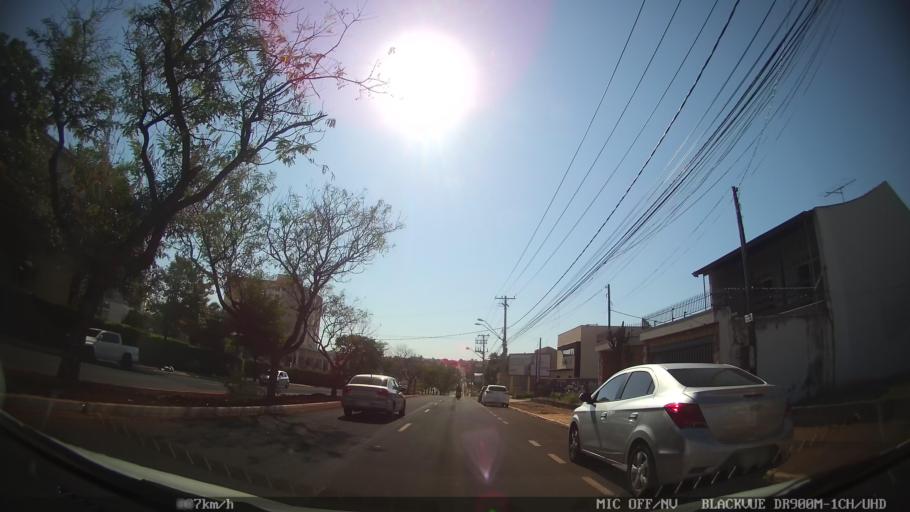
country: BR
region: Sao Paulo
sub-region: Ribeirao Preto
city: Ribeirao Preto
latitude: -21.2058
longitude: -47.8216
